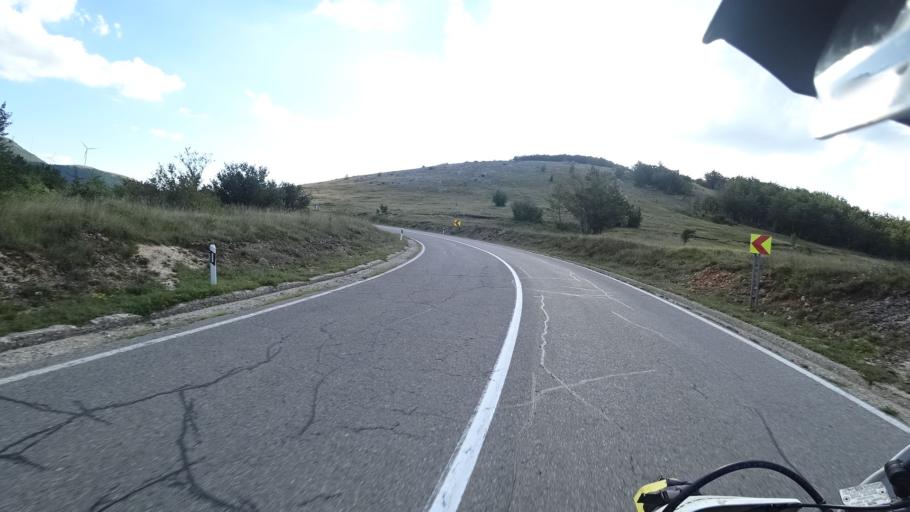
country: HR
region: Zadarska
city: Gracac
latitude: 44.2996
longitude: 16.0889
